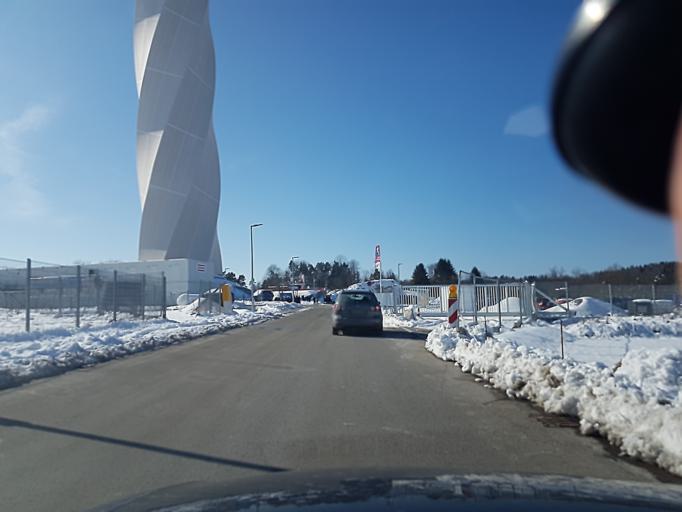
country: DE
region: Baden-Wuerttemberg
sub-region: Freiburg Region
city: Rottweil
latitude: 48.1799
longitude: 8.6270
